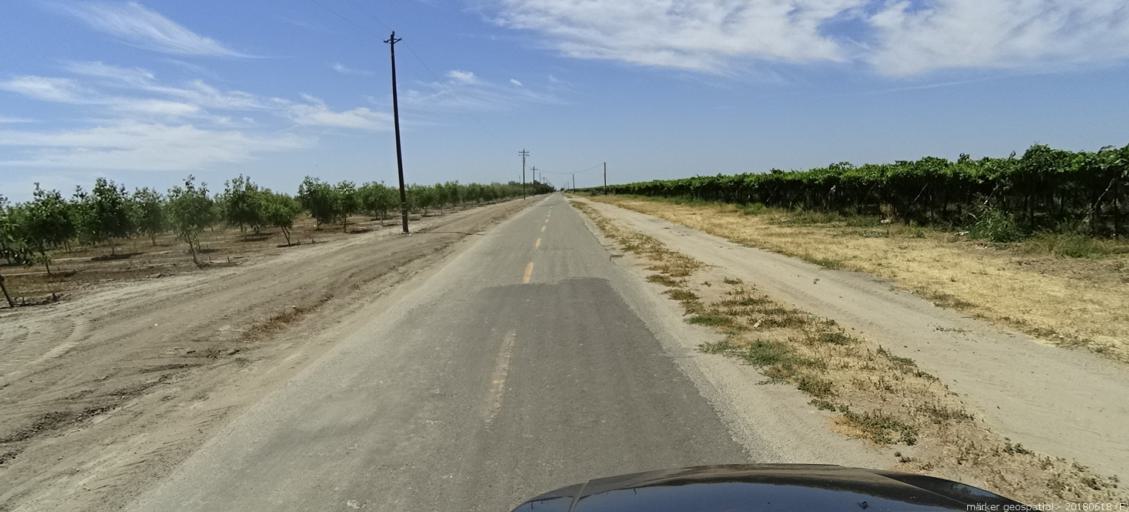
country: US
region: California
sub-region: Madera County
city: Parkwood
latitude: 36.8760
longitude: -120.1195
